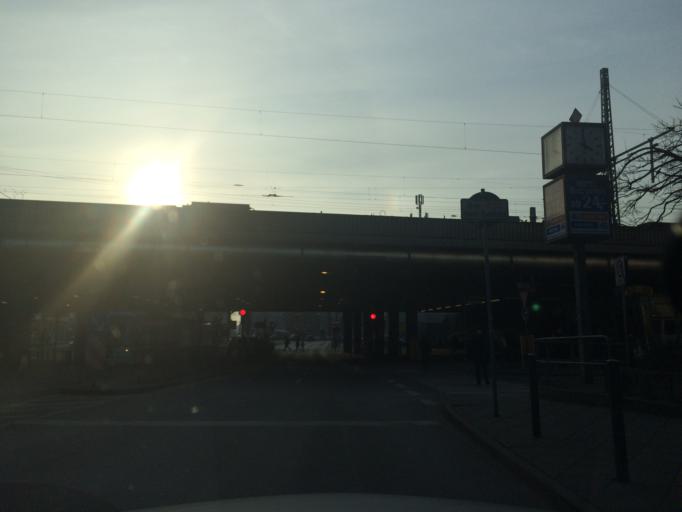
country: DE
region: Hesse
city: Niederrad
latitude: 50.1037
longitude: 8.6458
